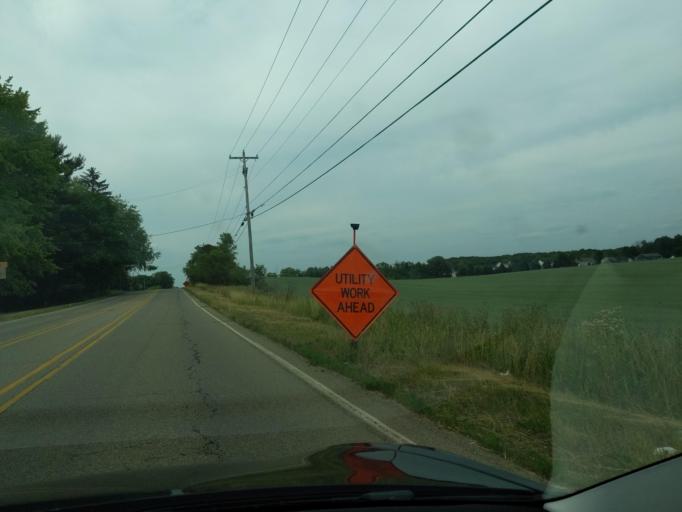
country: US
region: Michigan
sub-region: Clinton County
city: DeWitt
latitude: 42.8141
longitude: -84.6026
